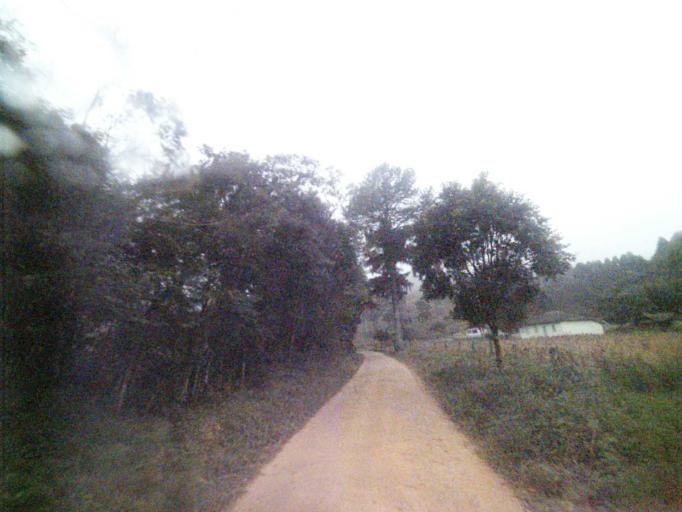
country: BR
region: Santa Catarina
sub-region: Anitapolis
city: Anitapolis
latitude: -27.8018
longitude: -49.1404
